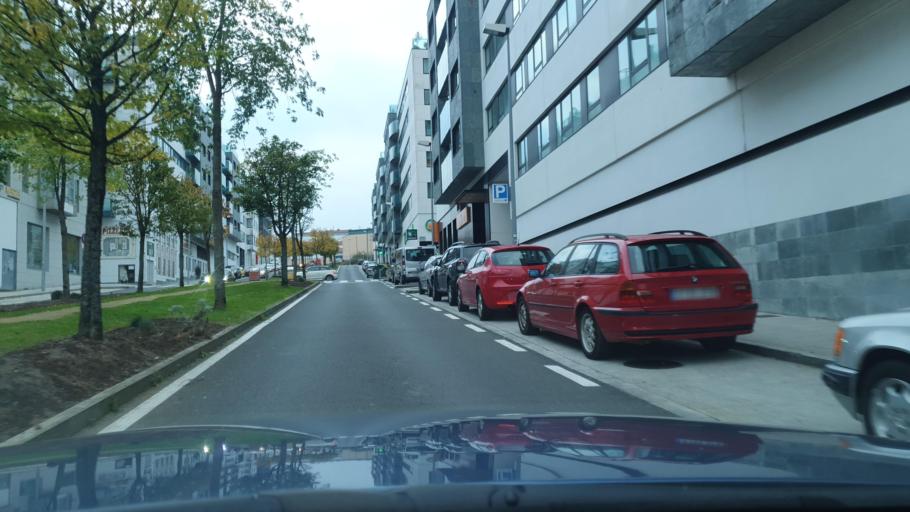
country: ES
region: Galicia
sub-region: Provincia da Coruna
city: Santiago de Compostela
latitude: 42.8684
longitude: -8.5597
